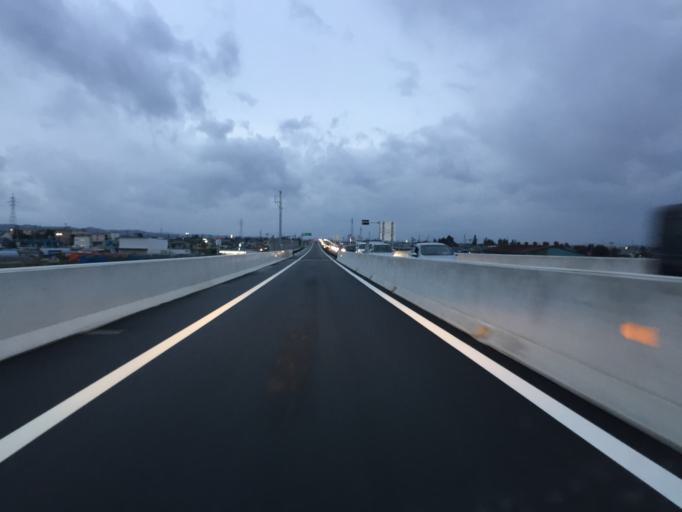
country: JP
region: Yamagata
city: Yonezawa
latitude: 37.9371
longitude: 140.1281
